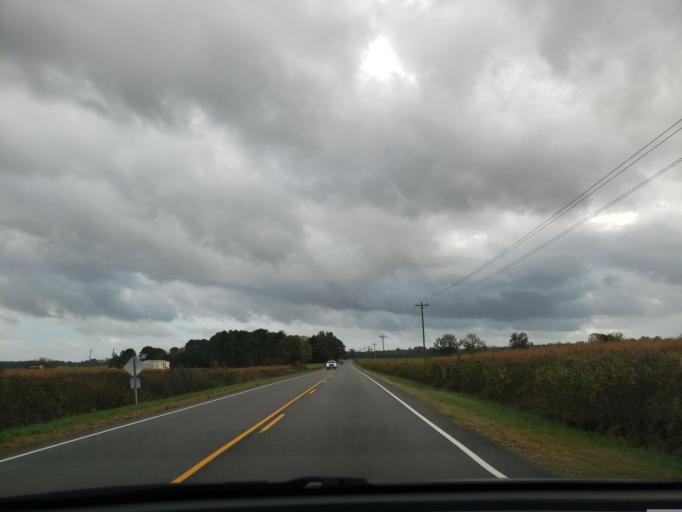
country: US
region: North Carolina
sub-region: Duplin County
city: Kenansville
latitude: 34.8965
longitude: -77.9103
